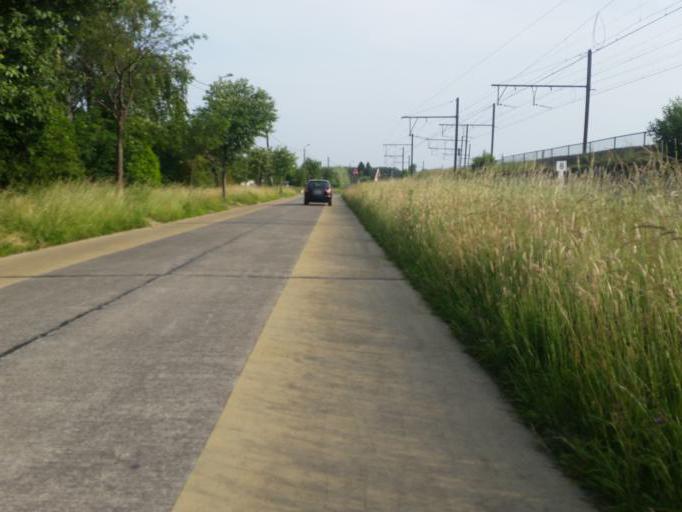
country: BE
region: Flanders
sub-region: Provincie Antwerpen
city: Duffel
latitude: 51.0647
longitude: 4.4967
